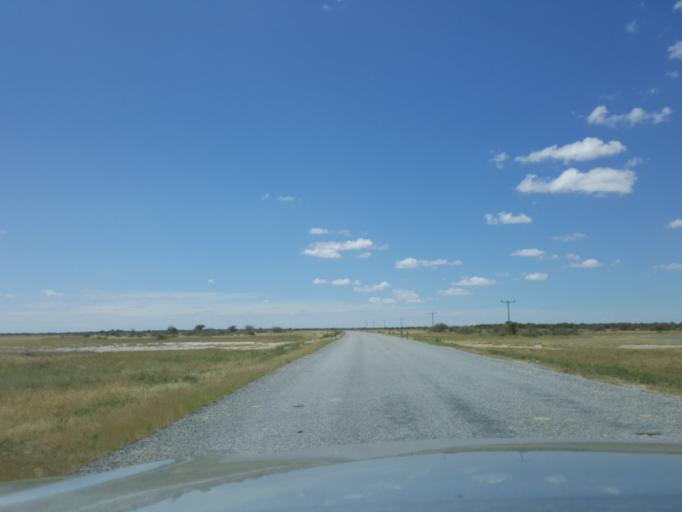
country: BW
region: Central
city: Gweta
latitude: -20.1391
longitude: 25.6704
